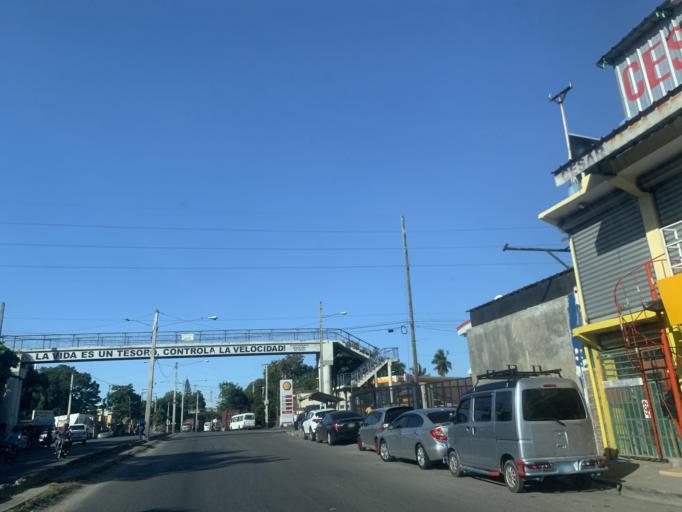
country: DO
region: San Cristobal
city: Bajos de Haina
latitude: 18.4315
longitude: -70.0263
